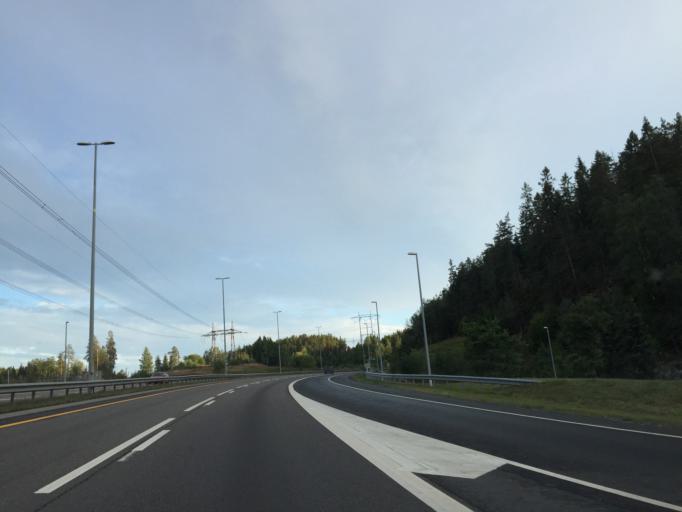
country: NO
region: Akershus
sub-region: Oppegard
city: Kolbotn
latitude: 59.8195
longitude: 10.8468
